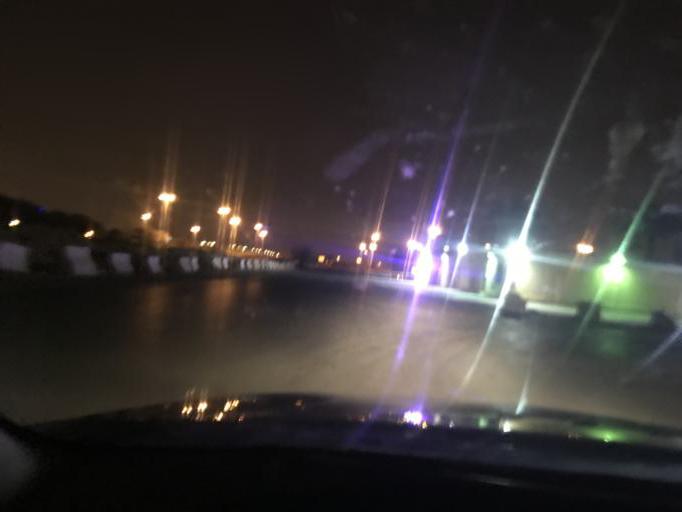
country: SA
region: Ar Riyad
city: Riyadh
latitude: 24.8110
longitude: 46.7182
